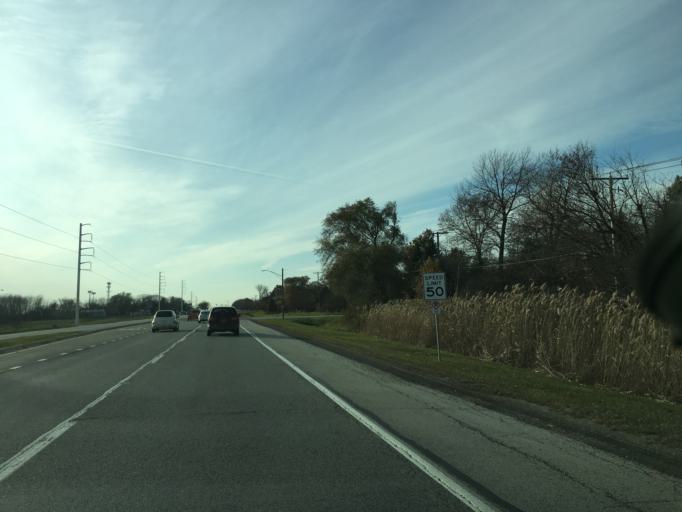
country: US
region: Illinois
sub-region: DuPage County
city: Woodridge
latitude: 41.7492
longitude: -88.0971
